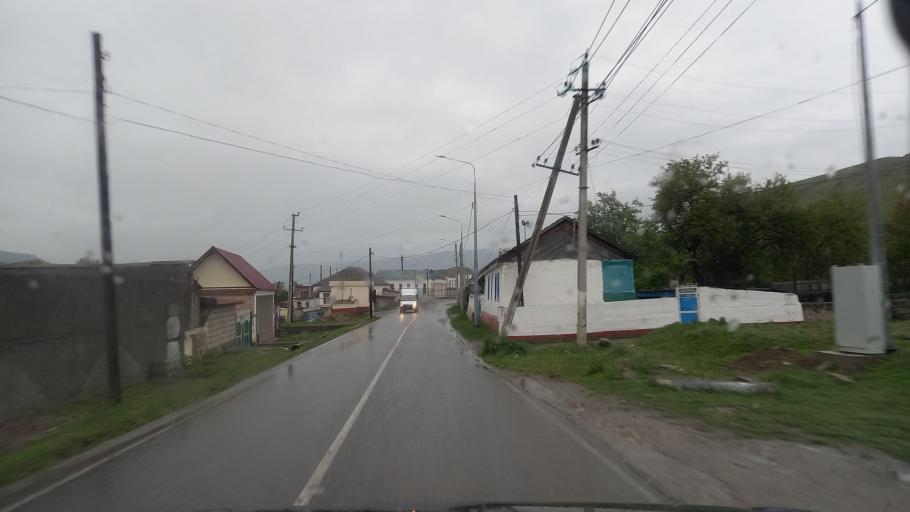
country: RU
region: Kabardino-Balkariya
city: Gundelen
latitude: 43.5940
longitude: 43.1808
